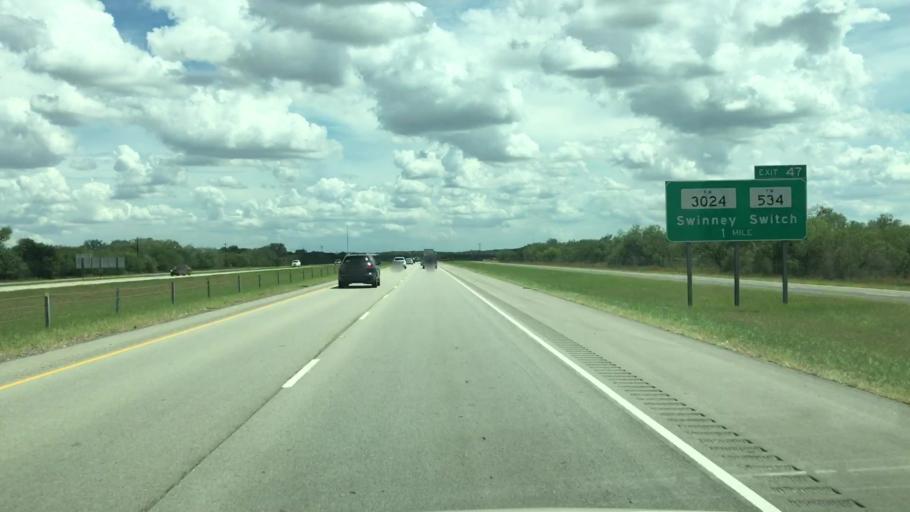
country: US
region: Texas
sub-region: Live Oak County
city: George West
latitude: 28.2751
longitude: -97.9492
